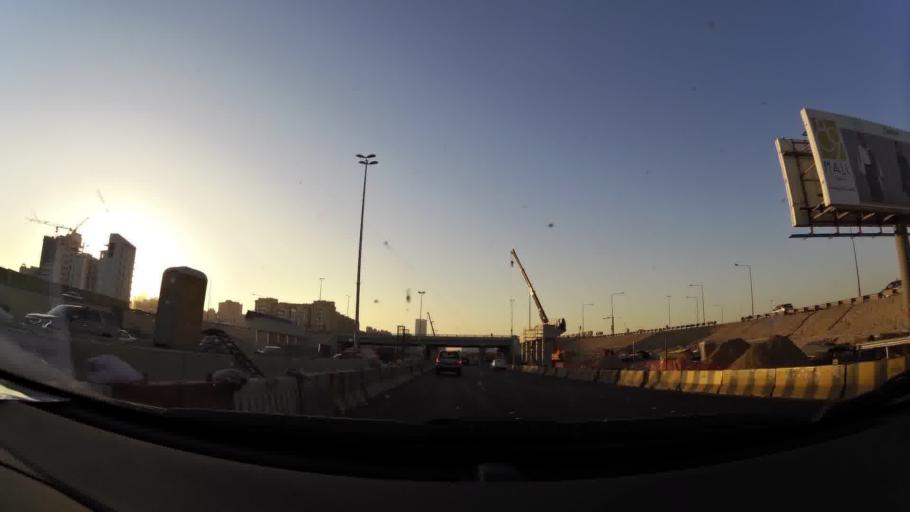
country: KW
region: Al Ahmadi
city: Al Fintas
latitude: 29.1854
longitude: 48.1116
